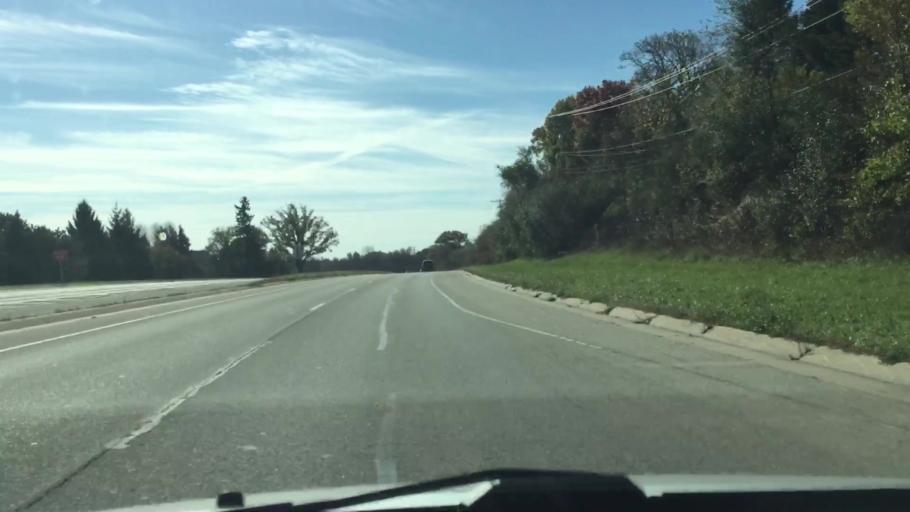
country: US
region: Wisconsin
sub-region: Waukesha County
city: Pewaukee
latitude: 43.1001
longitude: -88.2443
